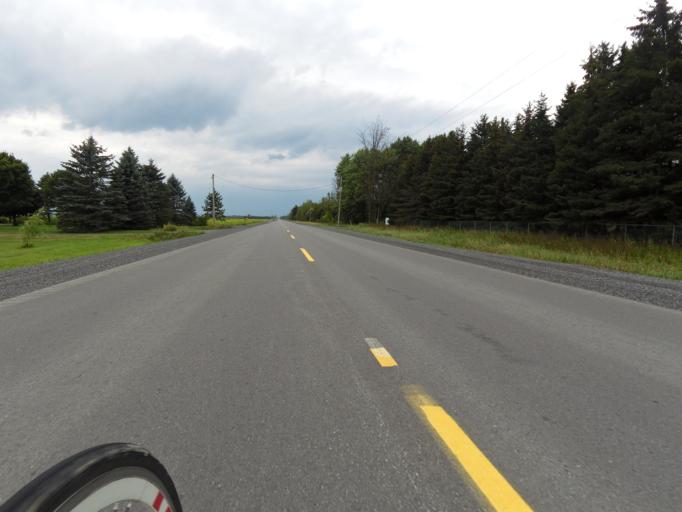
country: CA
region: Ontario
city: Bells Corners
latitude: 45.2100
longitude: -75.7684
